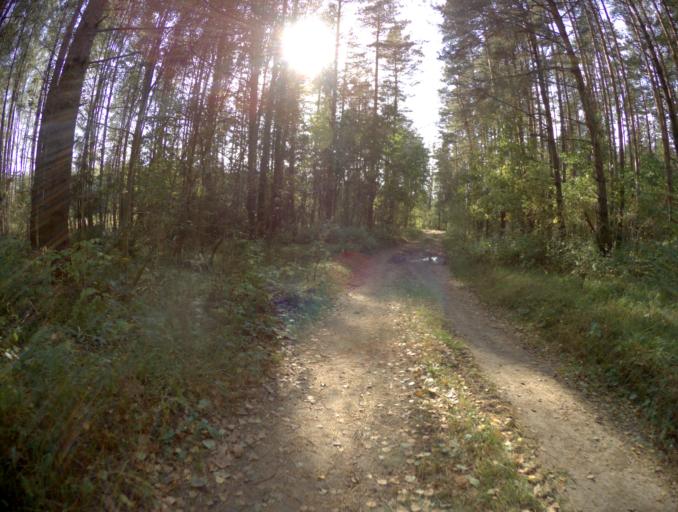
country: RU
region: Vladimir
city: Raduzhnyy
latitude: 56.0149
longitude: 40.2812
